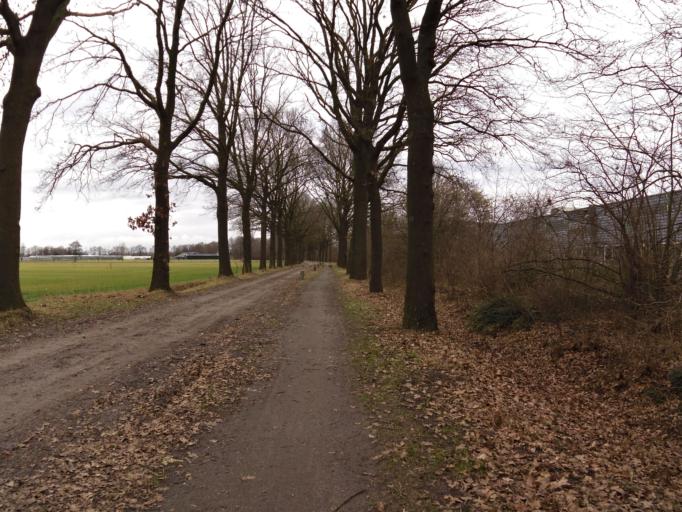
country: NL
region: North Brabant
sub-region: Gemeente Boxtel
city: Boxtel
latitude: 51.5803
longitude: 5.3056
